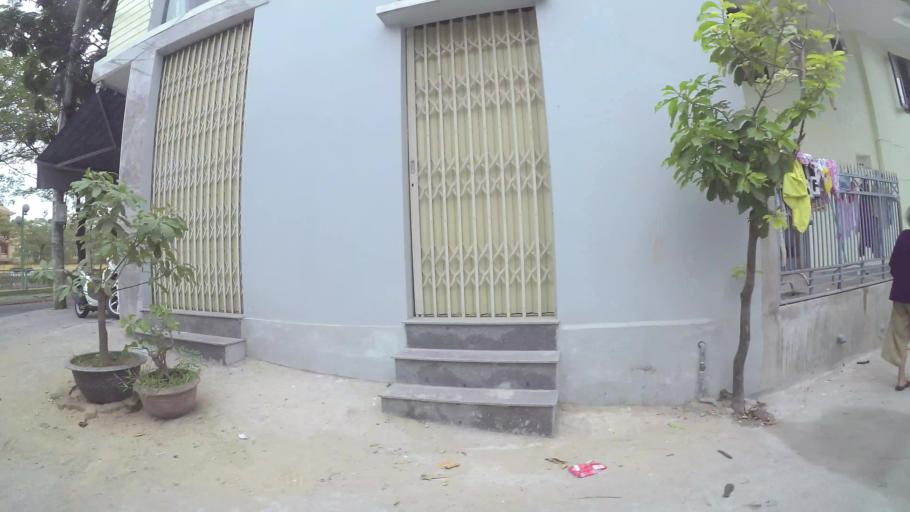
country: VN
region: Da Nang
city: Thanh Khe
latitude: 16.0701
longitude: 108.1828
